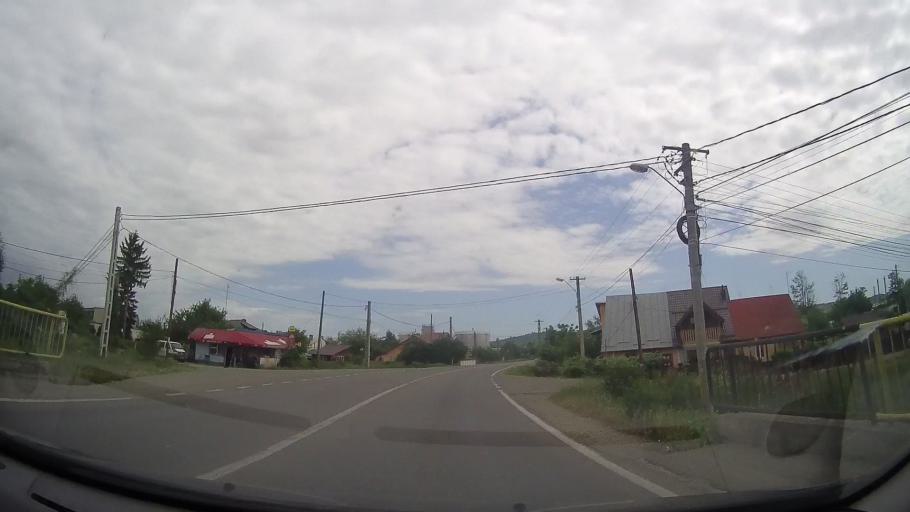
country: RO
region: Prahova
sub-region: Comuna Blejoiu
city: Blejoi
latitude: 45.0145
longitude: 26.0128
